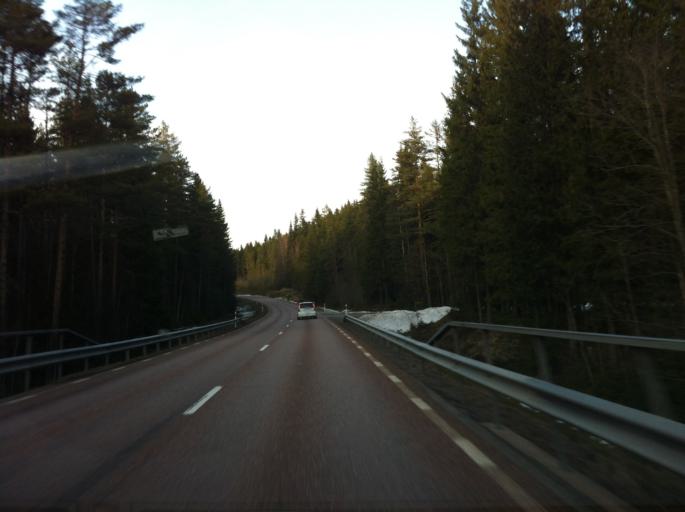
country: SE
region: Dalarna
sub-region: Vansbro Kommun
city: Vansbro
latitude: 60.4177
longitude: 14.2328
